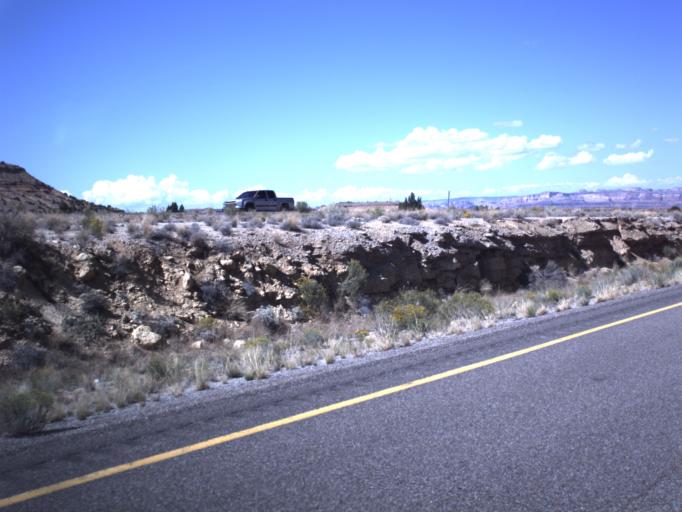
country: US
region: Utah
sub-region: Emery County
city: Castle Dale
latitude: 38.9179
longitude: -110.5014
